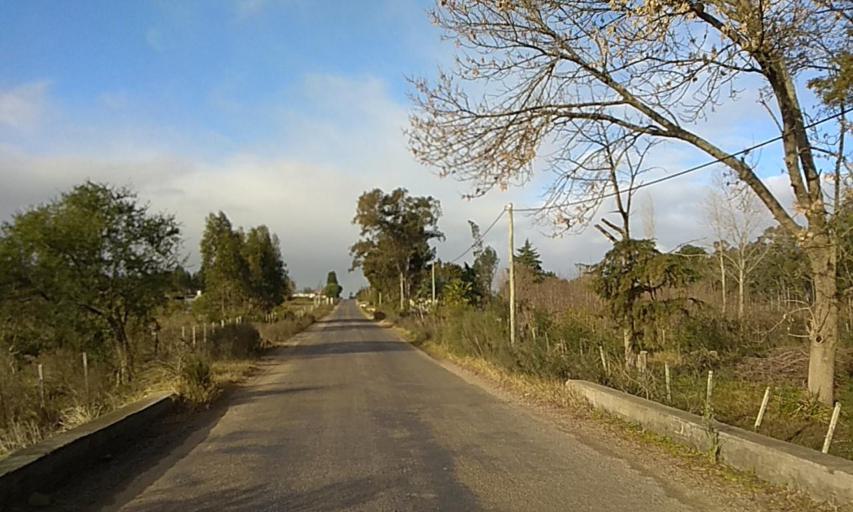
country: UY
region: Florida
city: Florida
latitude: -34.0432
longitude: -56.2000
